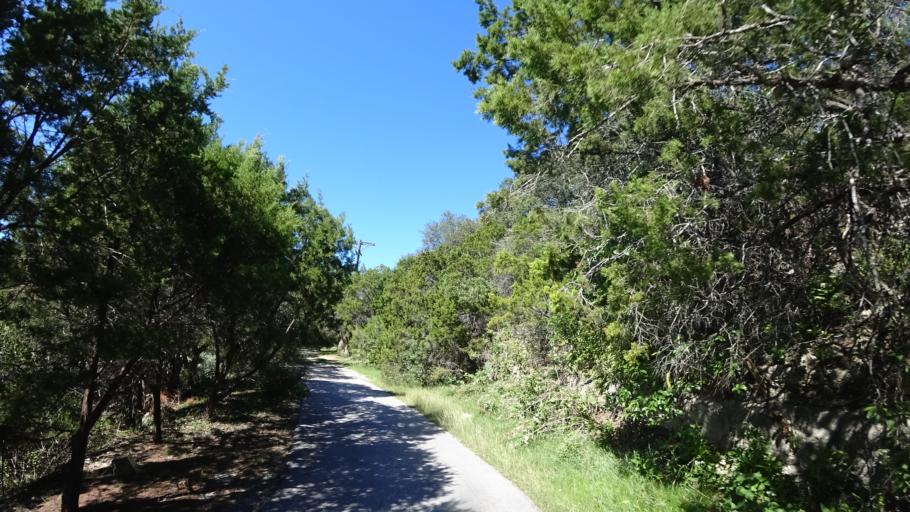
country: US
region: Texas
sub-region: Travis County
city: West Lake Hills
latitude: 30.3145
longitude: -97.7978
